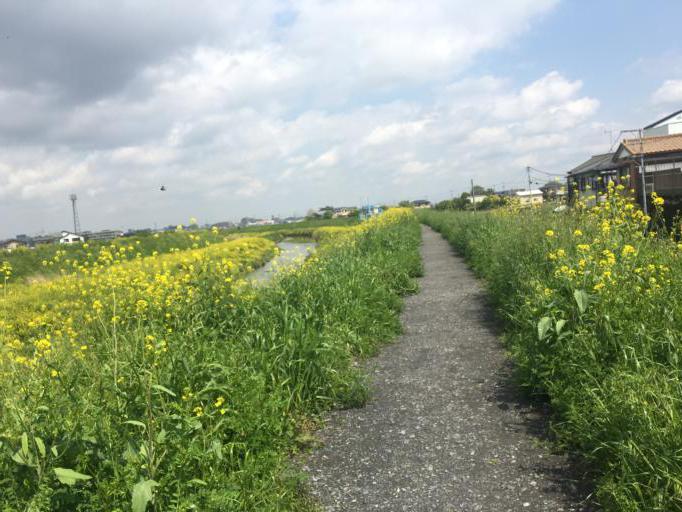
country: JP
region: Saitama
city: Kawagoe
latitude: 35.8943
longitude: 139.5047
